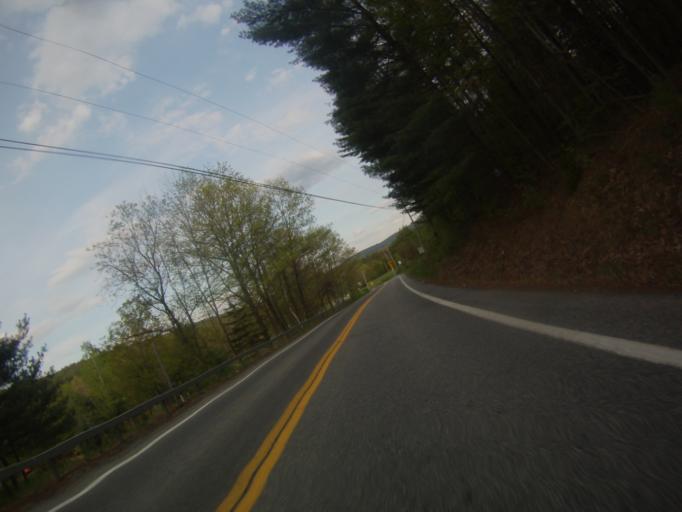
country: US
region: New York
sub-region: Essex County
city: Ticonderoga
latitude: 43.7564
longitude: -73.5133
